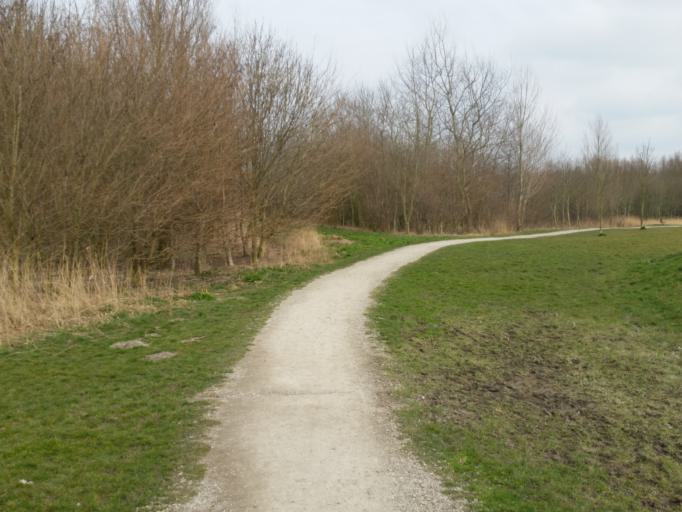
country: NL
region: South Holland
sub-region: Gemeente Delft
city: Delft
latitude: 51.9759
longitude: 4.3641
